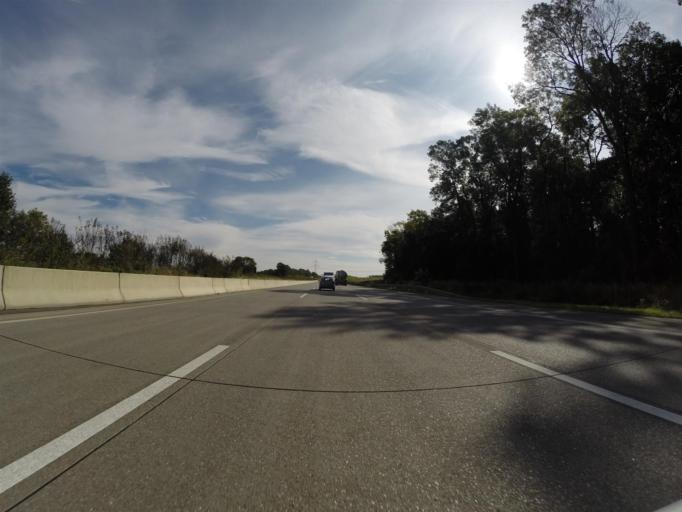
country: DE
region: Thuringia
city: Thonhausen
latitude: 50.8544
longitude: 12.3235
